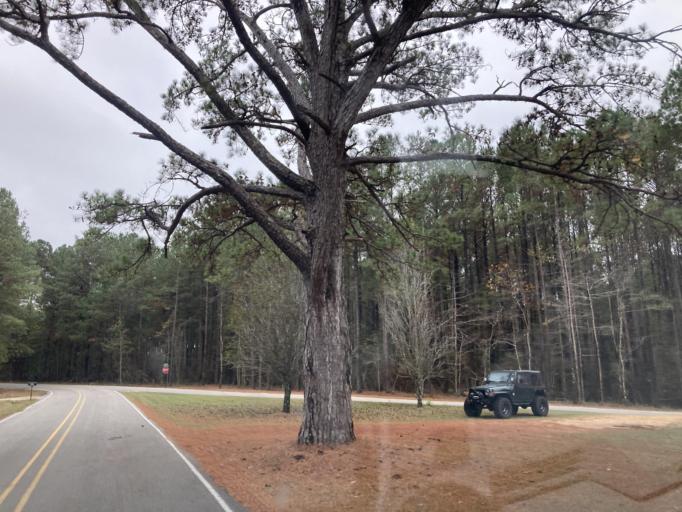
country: US
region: Mississippi
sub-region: Lamar County
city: Purvis
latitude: 31.1852
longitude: -89.4231
